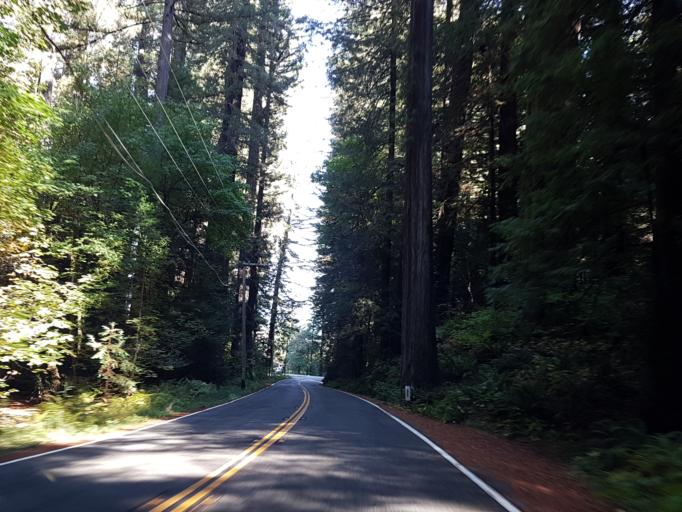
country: US
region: California
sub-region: Humboldt County
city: Rio Dell
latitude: 40.4162
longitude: -123.9697
